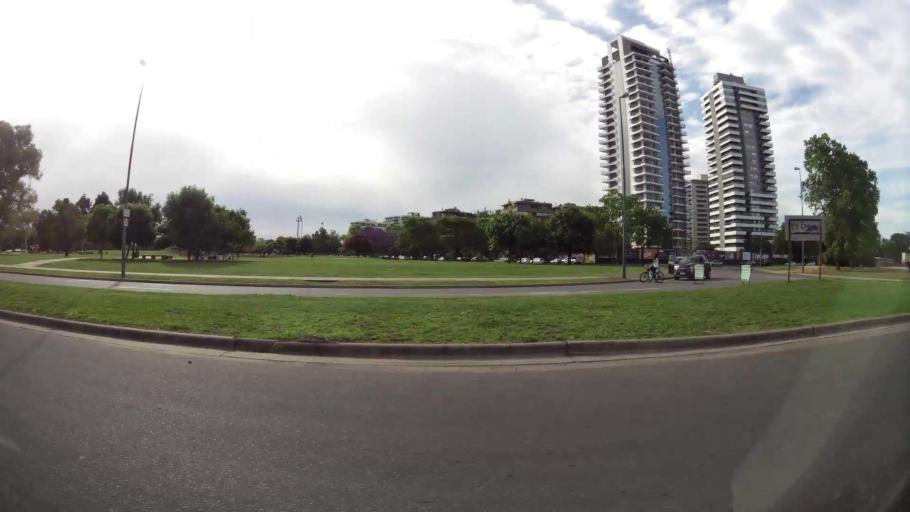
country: AR
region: Santa Fe
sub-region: Departamento de Rosario
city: Rosario
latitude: -32.9299
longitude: -60.6629
